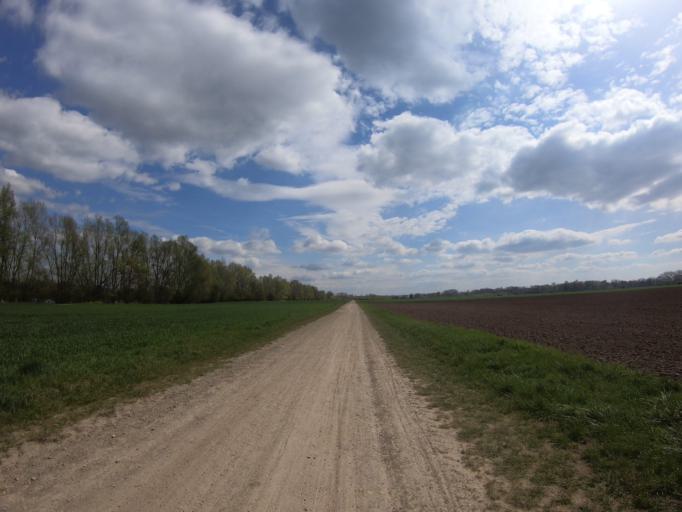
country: DE
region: Lower Saxony
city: Sarstedt
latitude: 52.2584
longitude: 9.8227
